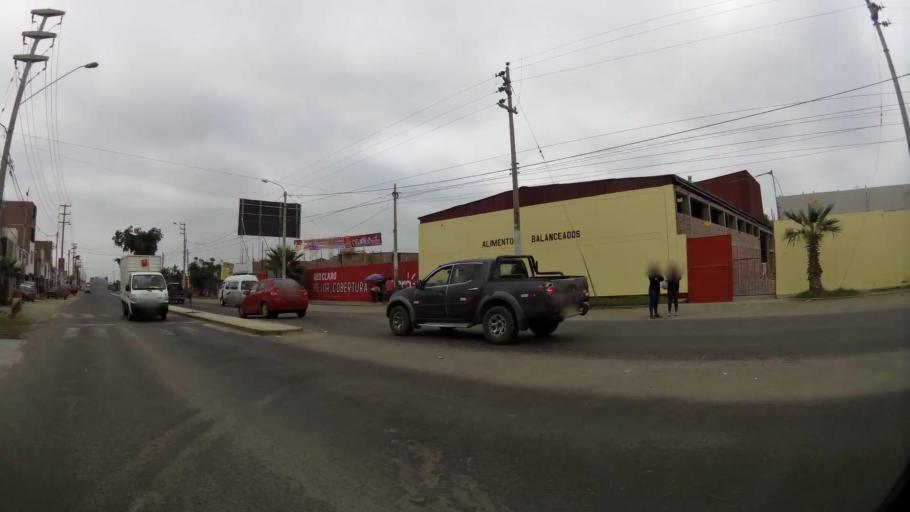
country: PE
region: La Libertad
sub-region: Provincia de Trujillo
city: La Esperanza
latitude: -8.0999
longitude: -79.0635
